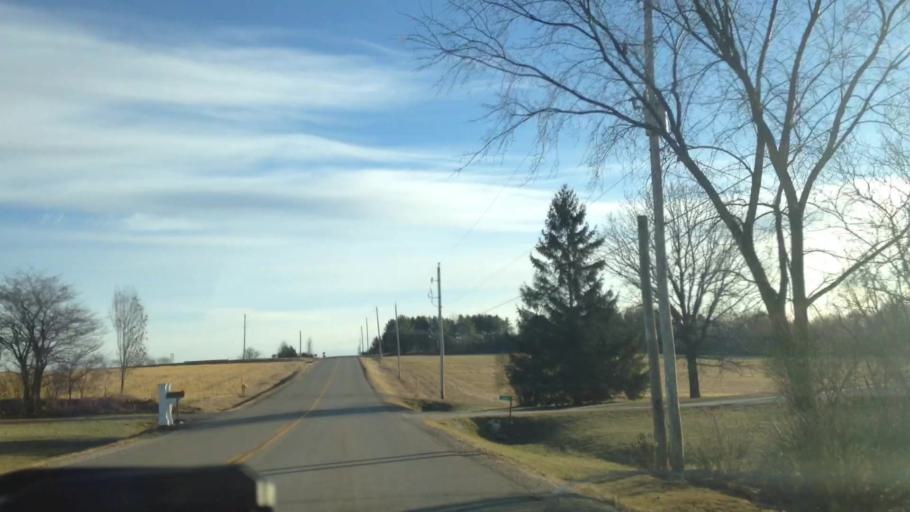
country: US
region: Wisconsin
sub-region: Washington County
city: Jackson
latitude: 43.2949
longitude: -88.1579
